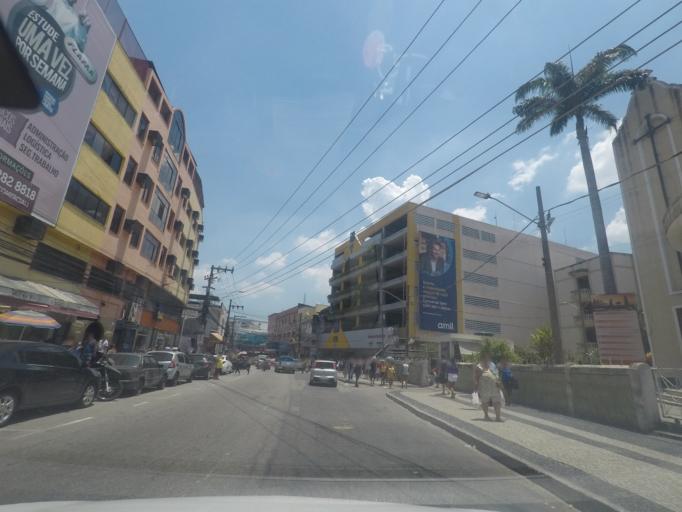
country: BR
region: Rio de Janeiro
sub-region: Duque De Caxias
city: Duque de Caxias
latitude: -22.7859
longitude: -43.3107
